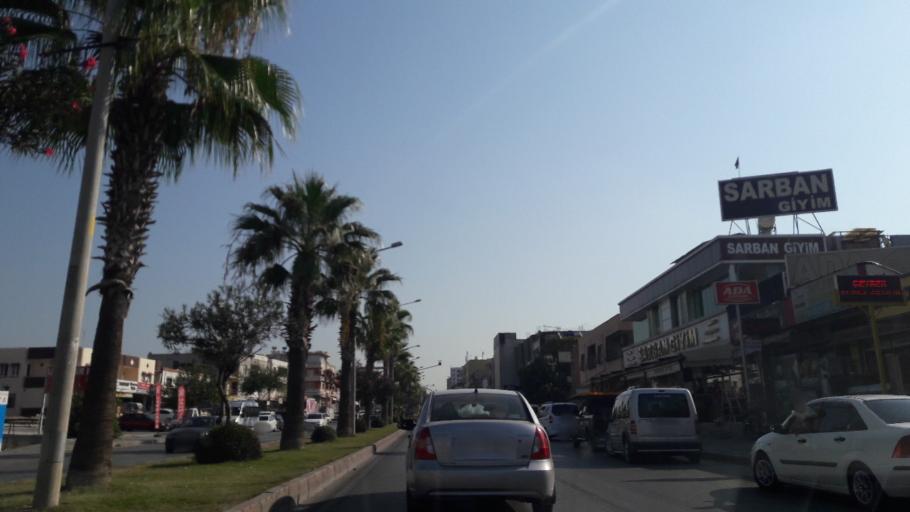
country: TR
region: Adana
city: Yuregir
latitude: 37.0348
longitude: 35.4161
